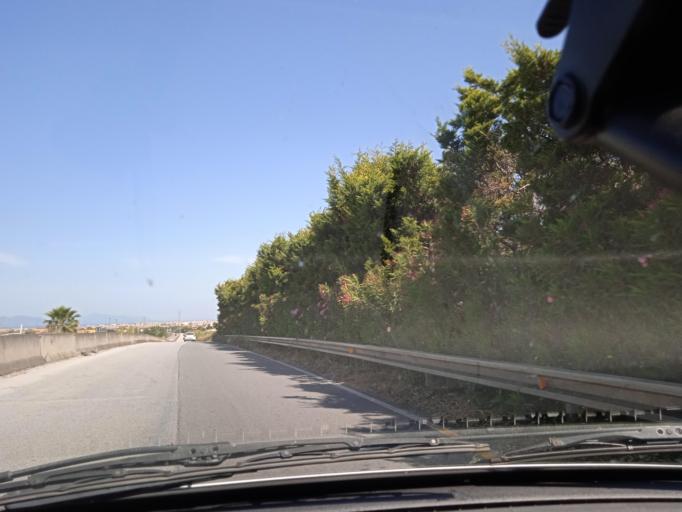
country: IT
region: Sicily
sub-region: Messina
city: San Filippo del Mela
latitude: 38.1874
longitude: 15.2633
